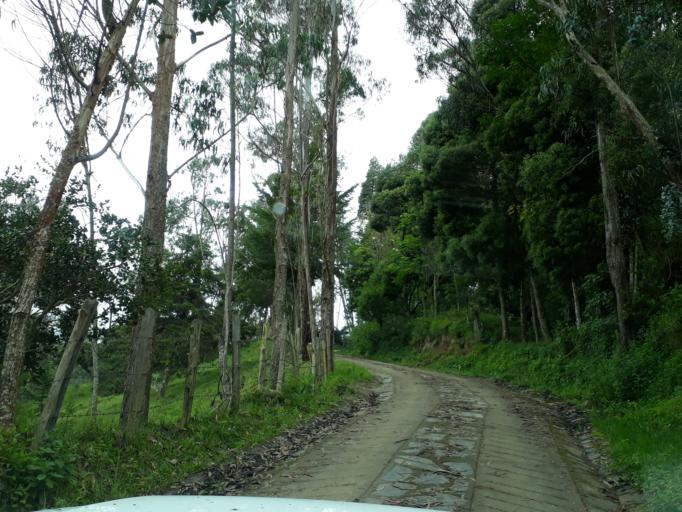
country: CO
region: Cundinamarca
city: Junin
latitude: 4.7810
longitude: -73.6452
